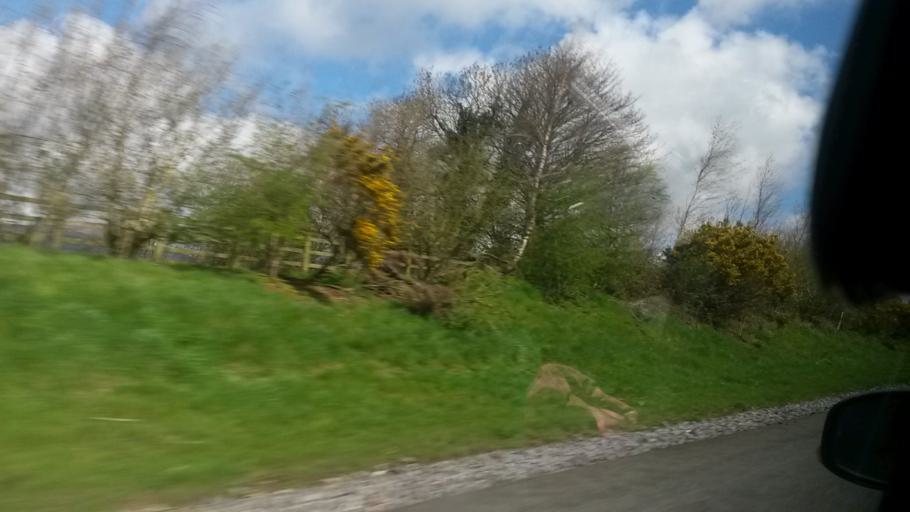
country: IE
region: Munster
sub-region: County Cork
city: Mitchelstown
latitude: 52.2971
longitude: -8.1843
